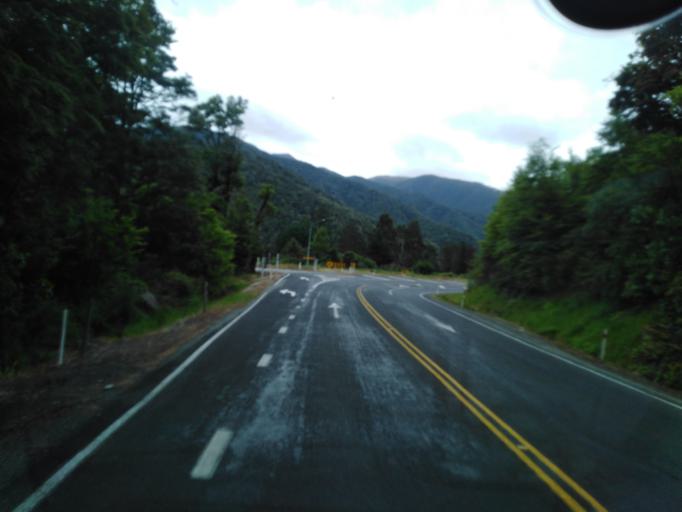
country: NZ
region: Tasman
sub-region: Tasman District
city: Wakefield
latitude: -41.7121
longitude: 172.5582
